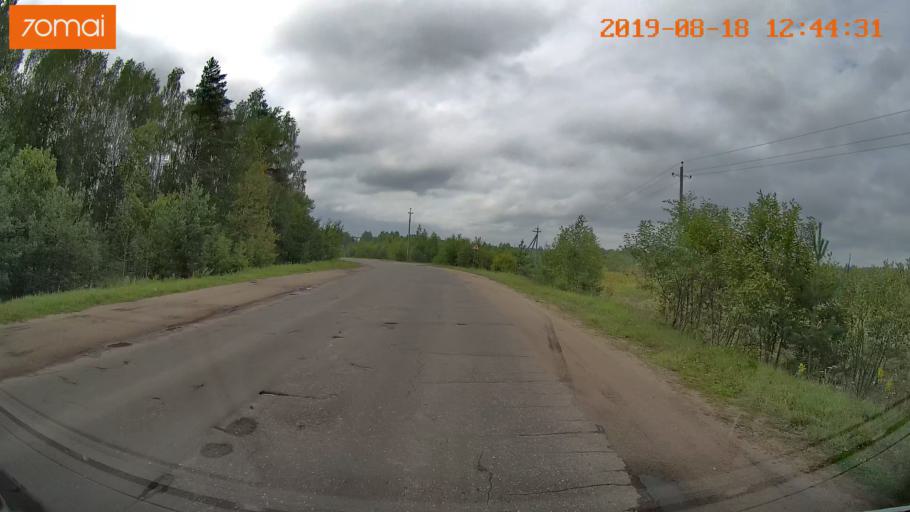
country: RU
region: Ivanovo
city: Novo-Talitsy
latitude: 57.0467
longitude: 40.8525
